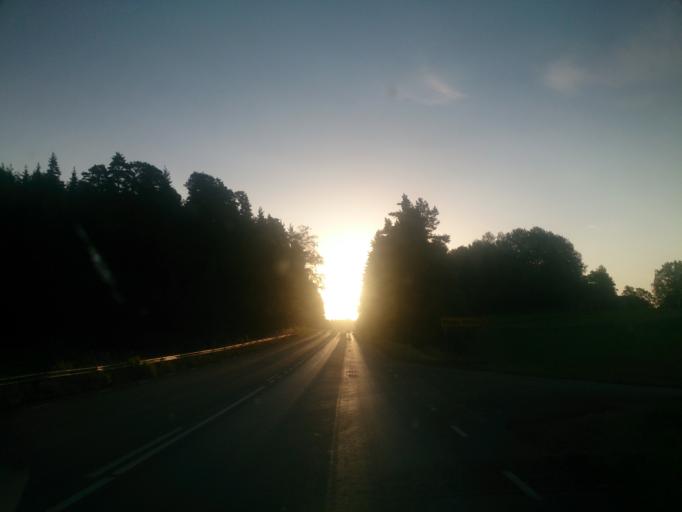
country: SE
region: Soedermanland
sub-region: Nykopings Kommun
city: Nykoping
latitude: 58.8668
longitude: 17.1547
